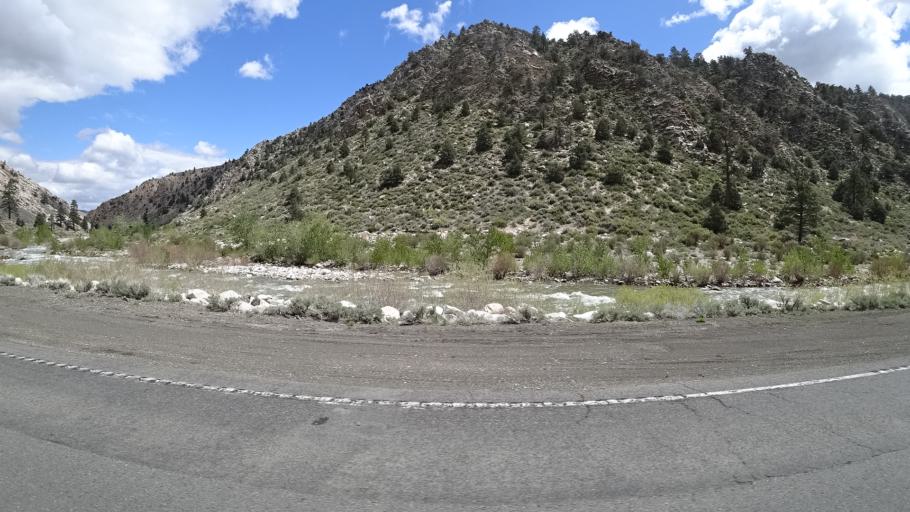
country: US
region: California
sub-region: Mono County
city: Bridgeport
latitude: 38.4649
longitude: -119.4630
